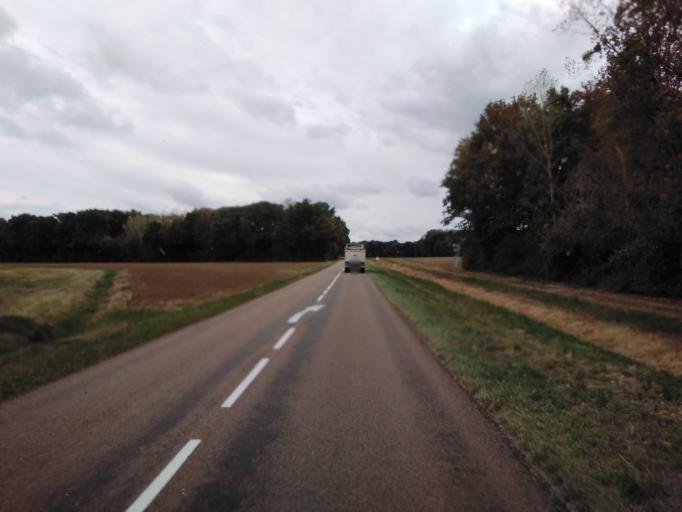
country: FR
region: Champagne-Ardenne
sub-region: Departement de l'Aube
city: Brienne-le-Chateau
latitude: 48.3321
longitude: 4.5259
